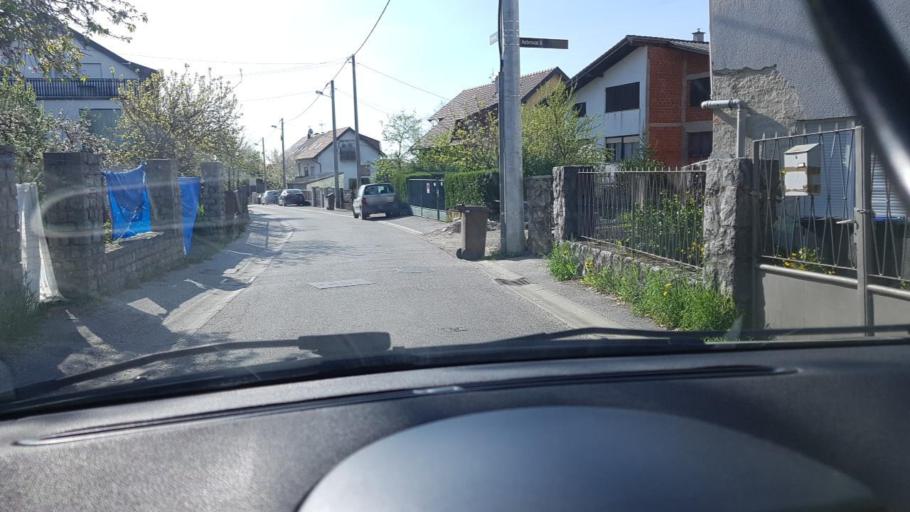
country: HR
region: Grad Zagreb
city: Zagreb
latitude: 45.8294
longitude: 16.0007
